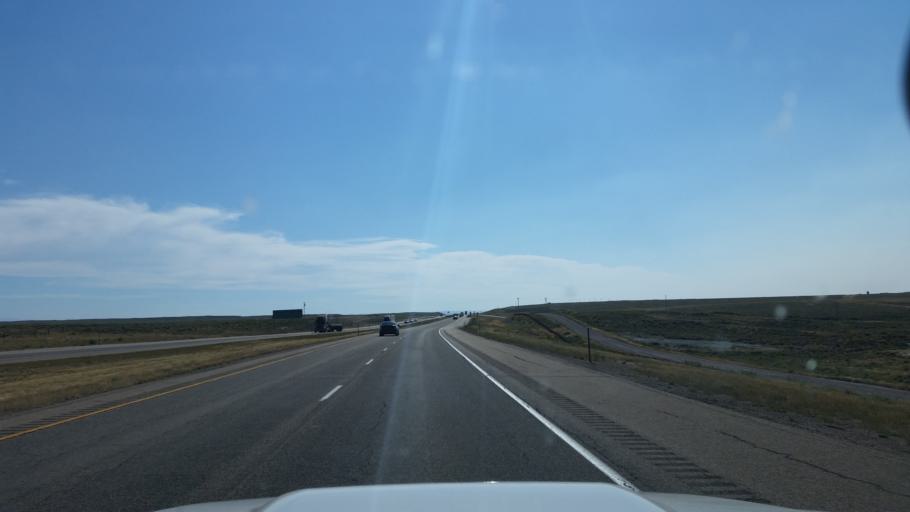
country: US
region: Wyoming
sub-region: Uinta County
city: Lyman
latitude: 41.4362
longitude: -110.1005
